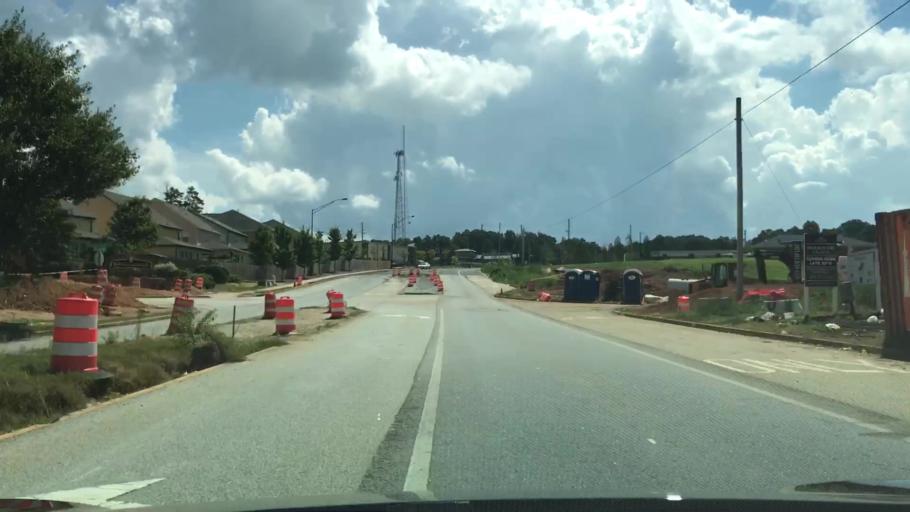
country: US
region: Georgia
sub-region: Gwinnett County
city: Snellville
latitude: 33.8533
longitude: -84.0464
